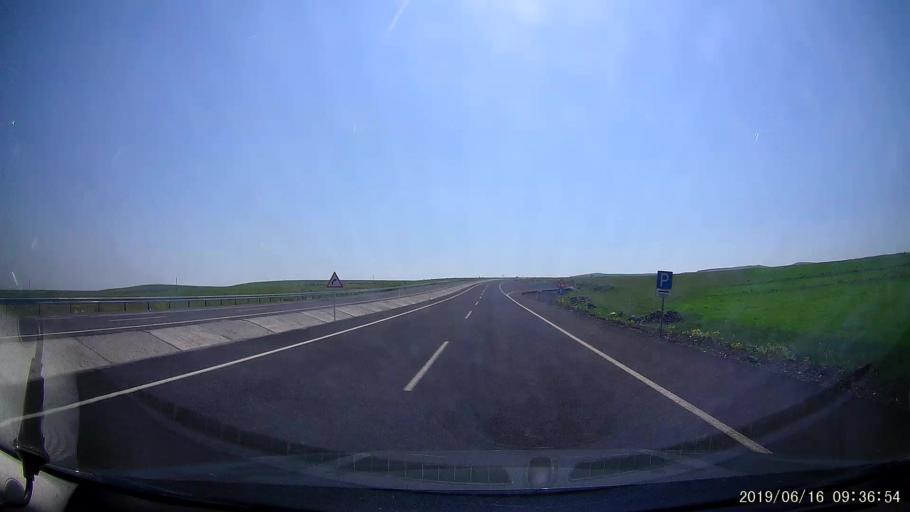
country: TR
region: Kars
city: Kars
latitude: 40.5555
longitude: 43.1826
